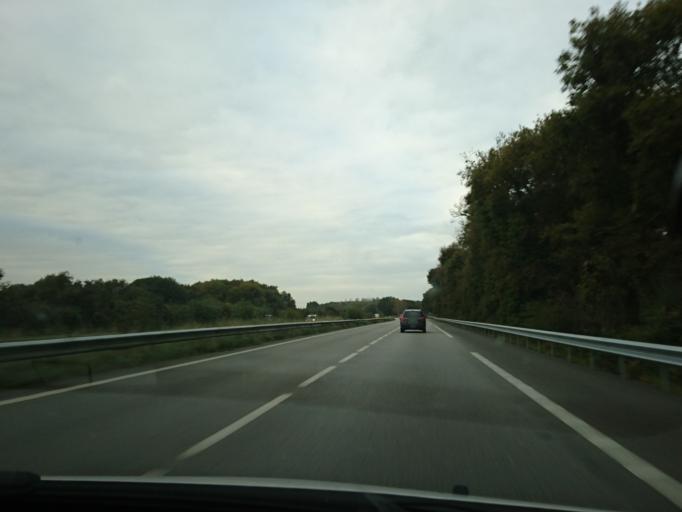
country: FR
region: Brittany
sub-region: Departement du Morbihan
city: Landaul
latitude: 47.7153
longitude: -3.0584
